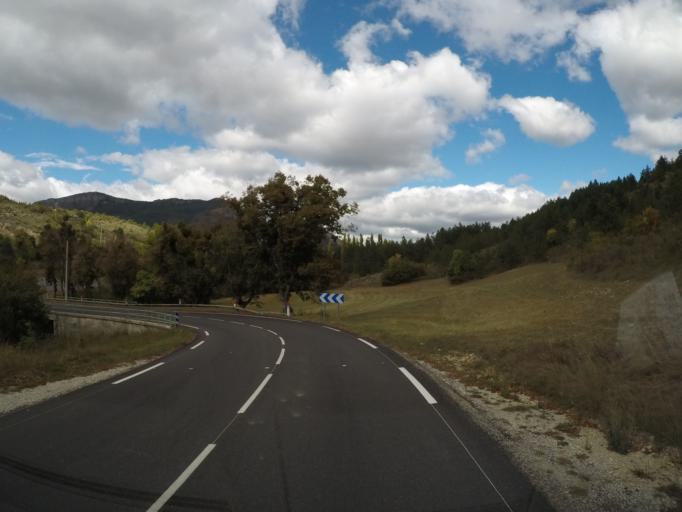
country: FR
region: Provence-Alpes-Cote d'Azur
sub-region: Departement du Vaucluse
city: Sault
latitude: 44.1874
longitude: 5.5395
